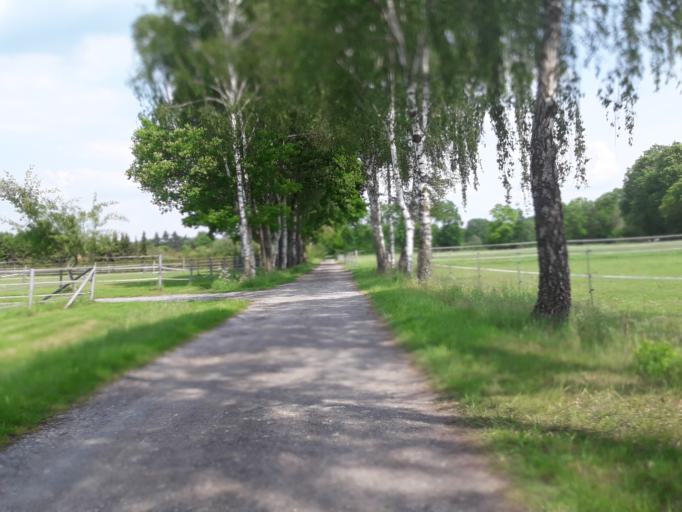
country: DE
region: North Rhine-Westphalia
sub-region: Regierungsbezirk Detmold
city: Paderborn
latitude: 51.7598
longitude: 8.7536
